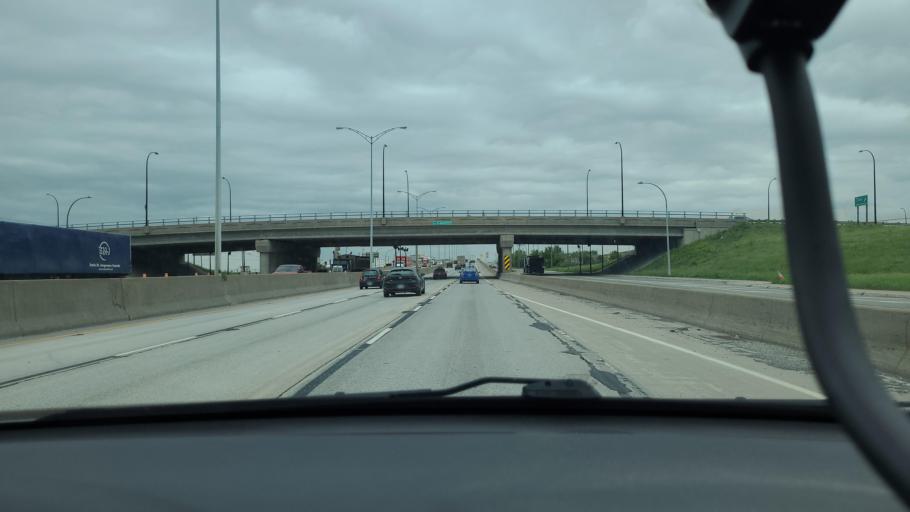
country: CA
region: Quebec
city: Montreal-Est
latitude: 45.6491
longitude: -73.5277
